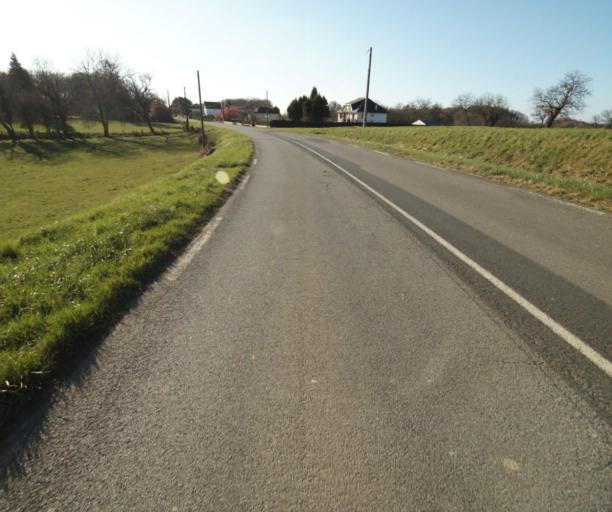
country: FR
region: Limousin
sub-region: Departement de la Correze
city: Seilhac
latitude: 45.3596
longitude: 1.7269
